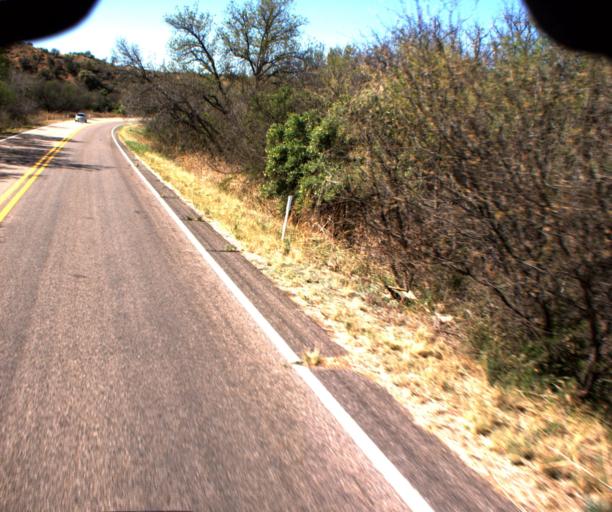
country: US
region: Arizona
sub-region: Santa Cruz County
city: Rio Rico
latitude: 31.5297
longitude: -110.7658
